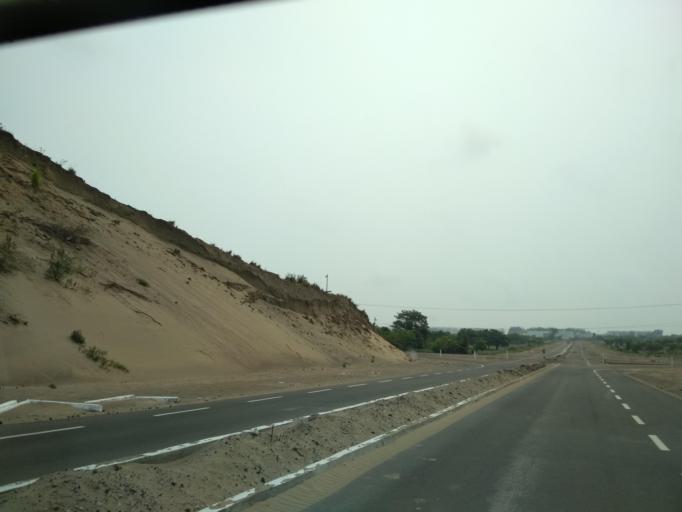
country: MX
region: Veracruz
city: Anton Lizardo
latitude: 19.0440
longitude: -95.9875
